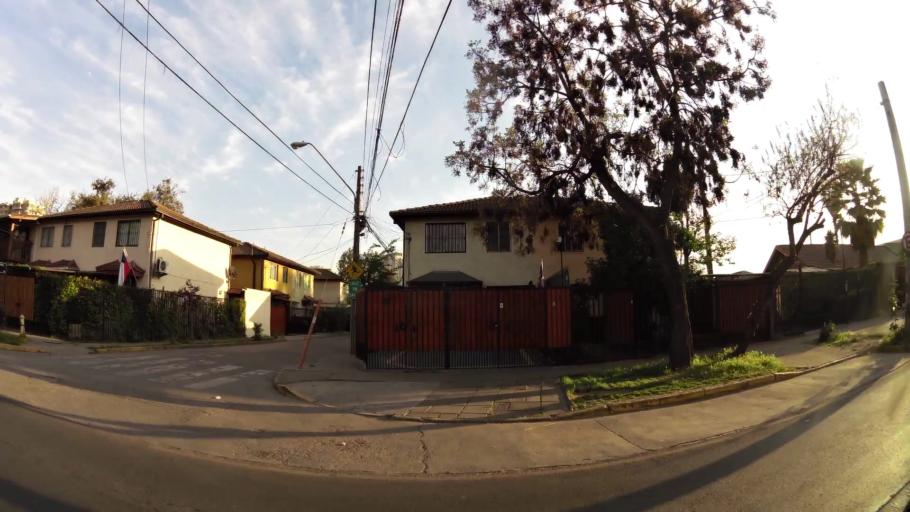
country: CL
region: Santiago Metropolitan
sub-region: Provincia de Santiago
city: Villa Presidente Frei, Nunoa, Santiago, Chile
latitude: -33.4600
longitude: -70.5743
